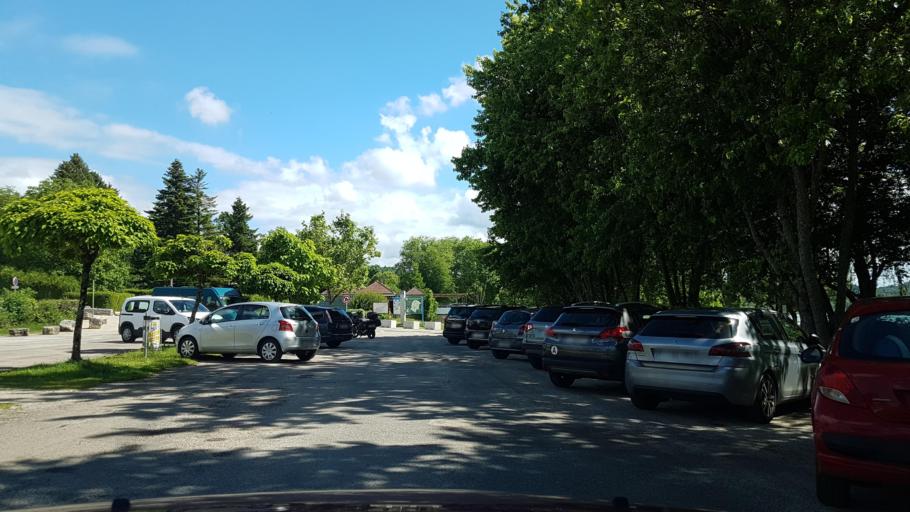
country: FR
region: Franche-Comte
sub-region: Departement du Jura
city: Clairvaux-les-Lacs
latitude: 46.5713
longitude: 5.7525
